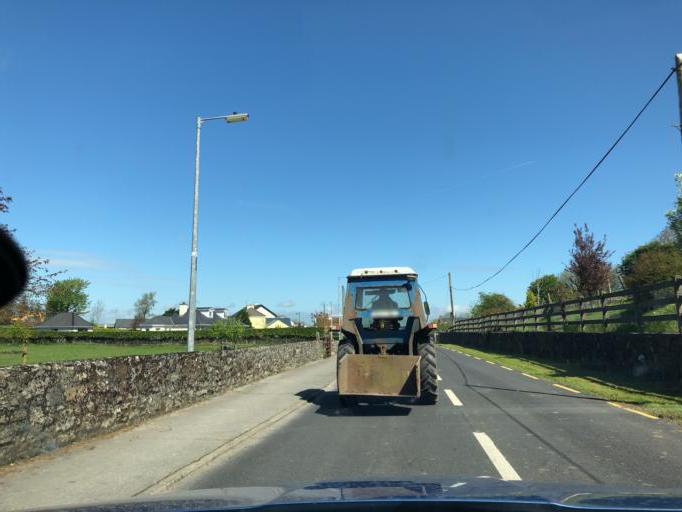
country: IE
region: Connaught
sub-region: County Galway
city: Portumna
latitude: 53.1481
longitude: -8.3721
